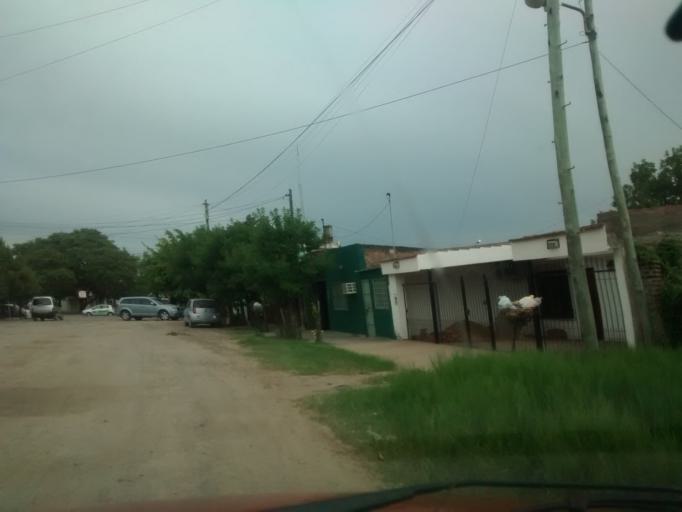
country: AR
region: Chaco
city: Resistencia
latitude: -27.4523
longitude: -59.0129
